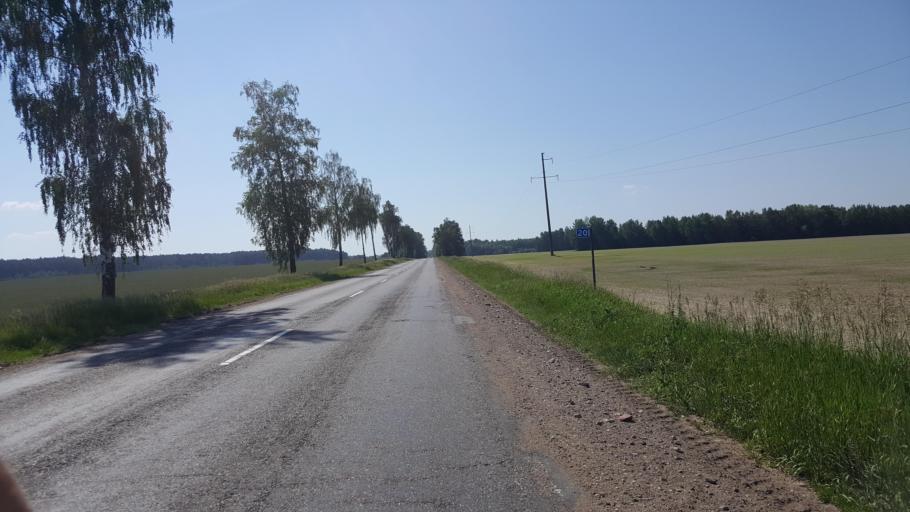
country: BY
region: Brest
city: Zhabinka
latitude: 52.2513
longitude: 23.9694
